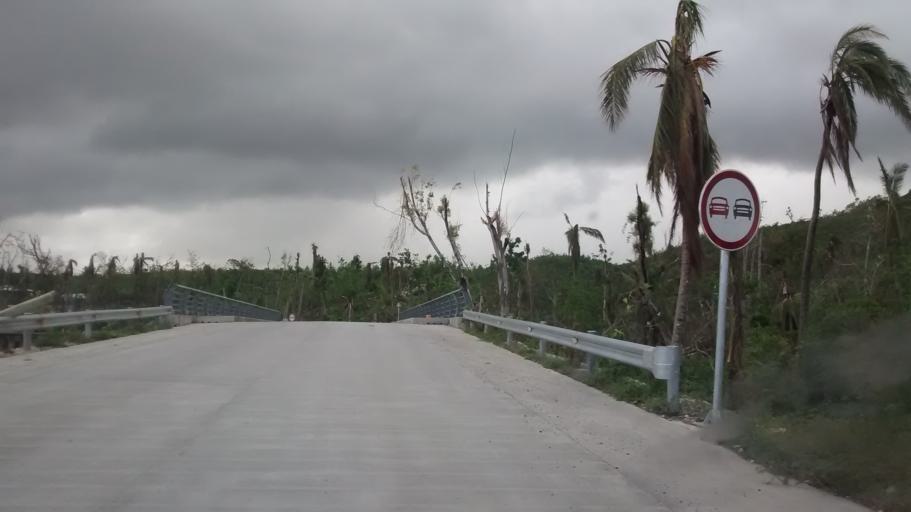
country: HT
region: Grandans
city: Jeremie
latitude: 18.6161
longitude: -74.0869
